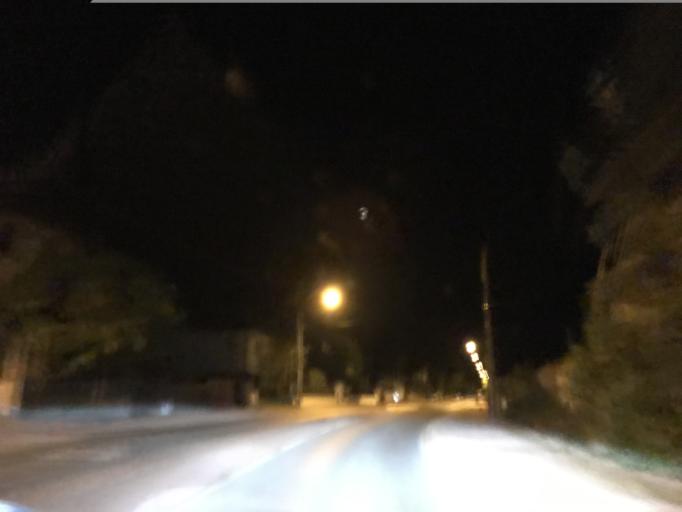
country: FR
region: Auvergne
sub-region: Departement de l'Allier
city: Abrest
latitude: 46.0947
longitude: 3.4504
